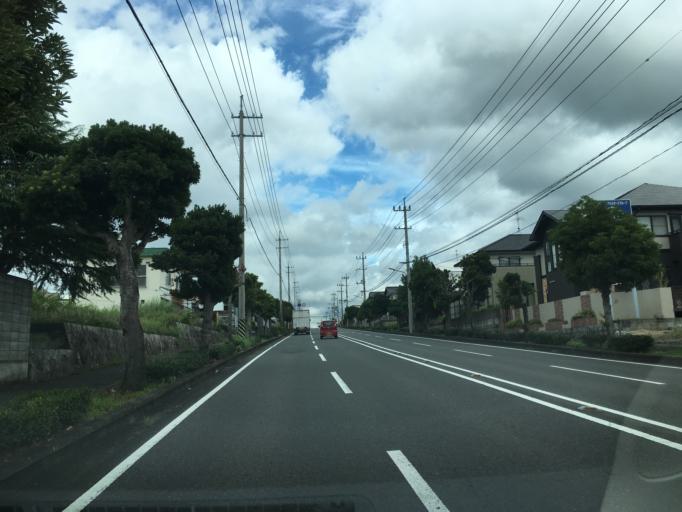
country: JP
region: Okayama
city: Okayama-shi
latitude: 34.7783
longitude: 134.0381
